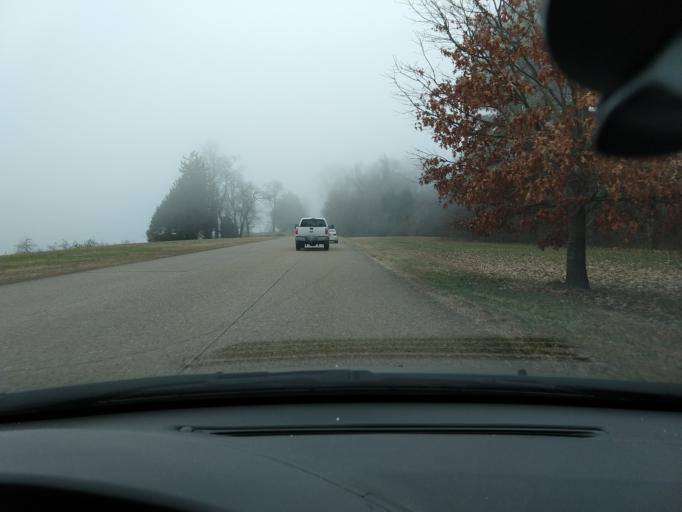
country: US
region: Virginia
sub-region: York County
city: Yorktown
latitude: 37.2715
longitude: -76.5762
